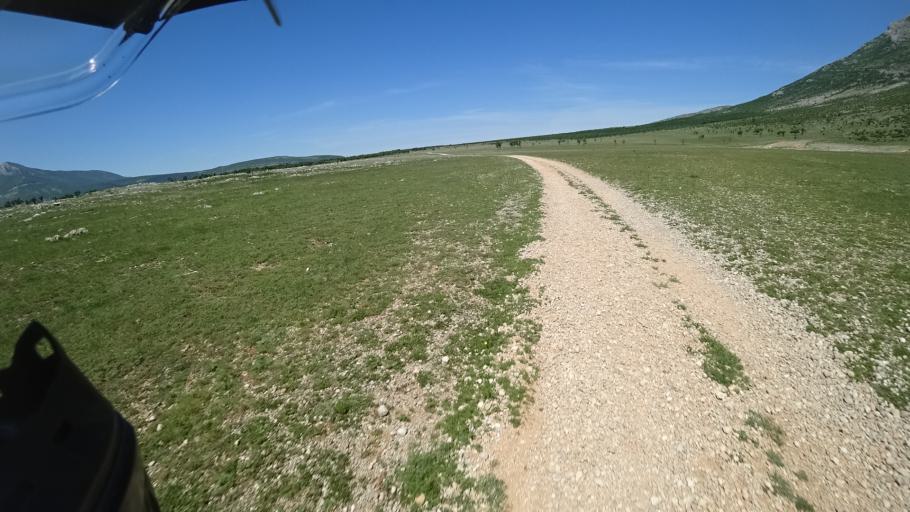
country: BA
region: Federation of Bosnia and Herzegovina
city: Bosansko Grahovo
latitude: 44.0037
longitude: 16.3984
